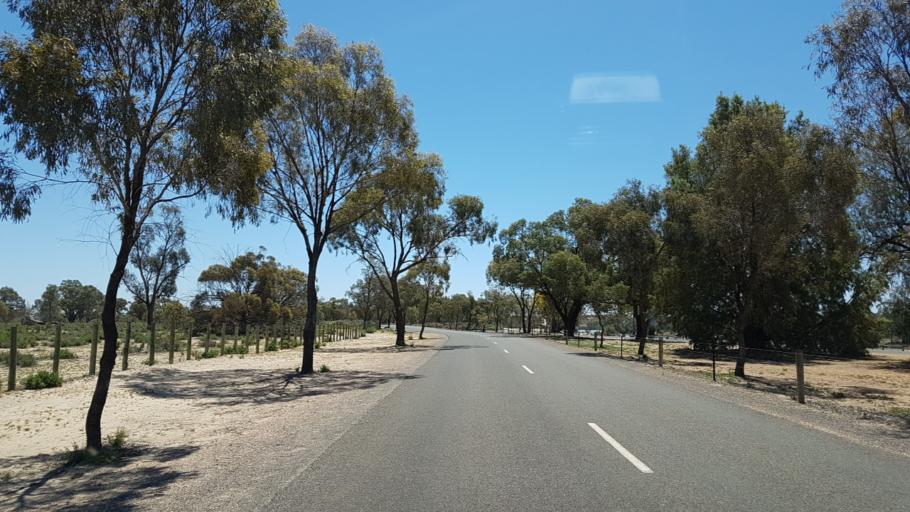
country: AU
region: South Australia
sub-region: Loxton Waikerie
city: Waikerie
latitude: -34.1718
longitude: 139.9796
